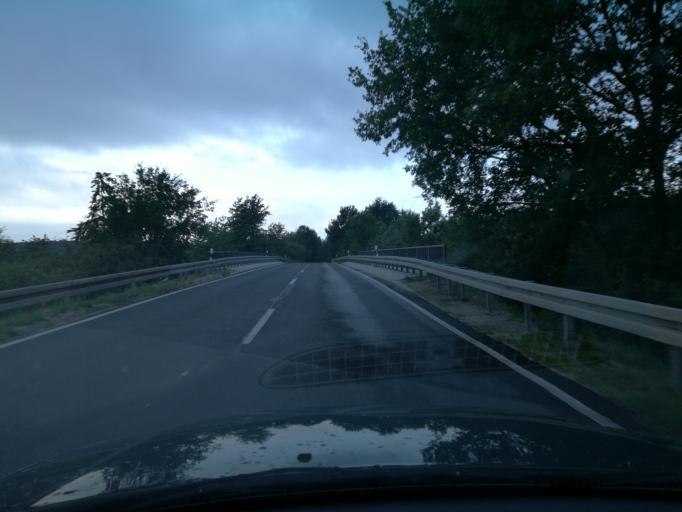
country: DE
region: Bavaria
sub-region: Regierungsbezirk Mittelfranken
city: Obermichelbach
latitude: 49.5601
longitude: 10.9557
